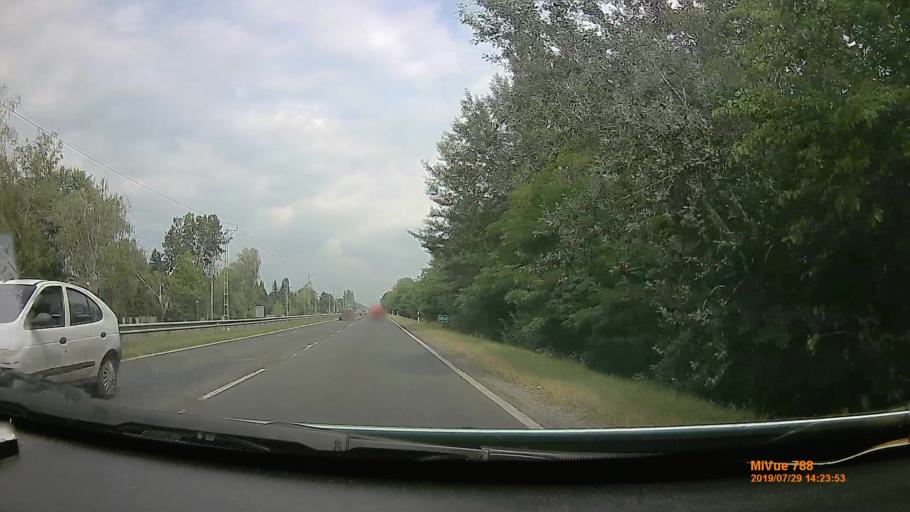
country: HU
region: Somogy
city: Siofok
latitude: 46.8949
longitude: 18.0074
